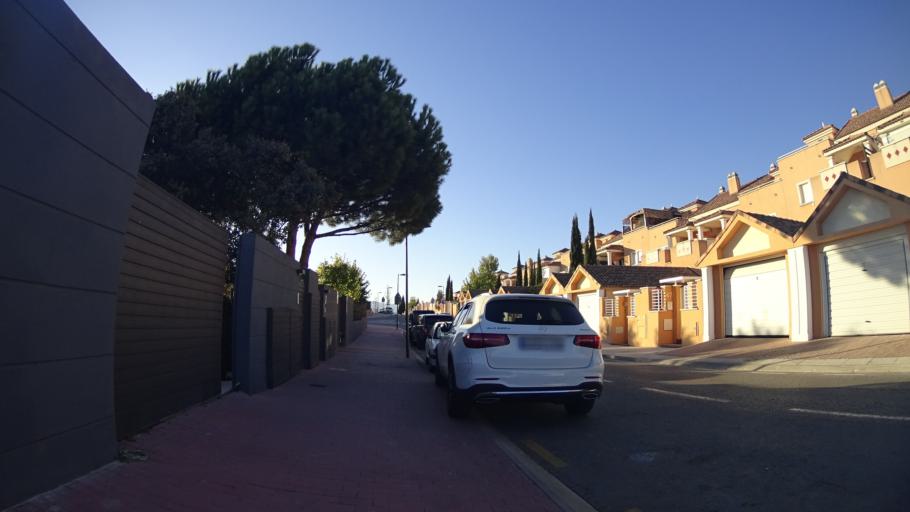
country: ES
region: Madrid
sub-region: Provincia de Madrid
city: Torrelodones
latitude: 40.5749
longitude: -3.9384
